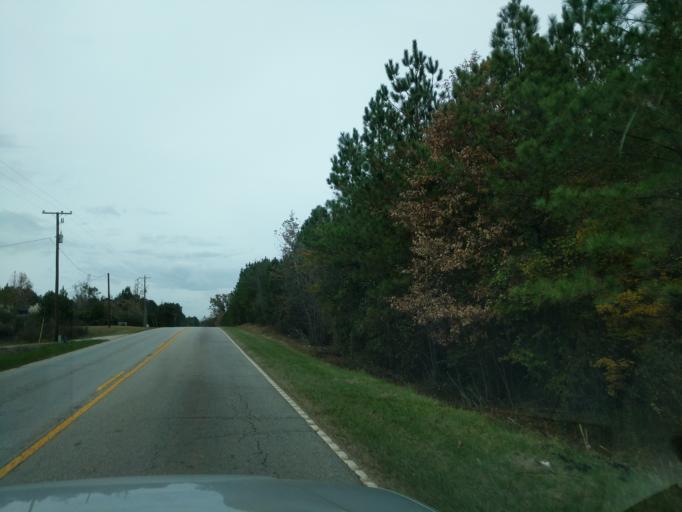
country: US
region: South Carolina
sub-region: Saluda County
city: Saluda
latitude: 34.0659
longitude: -81.7619
